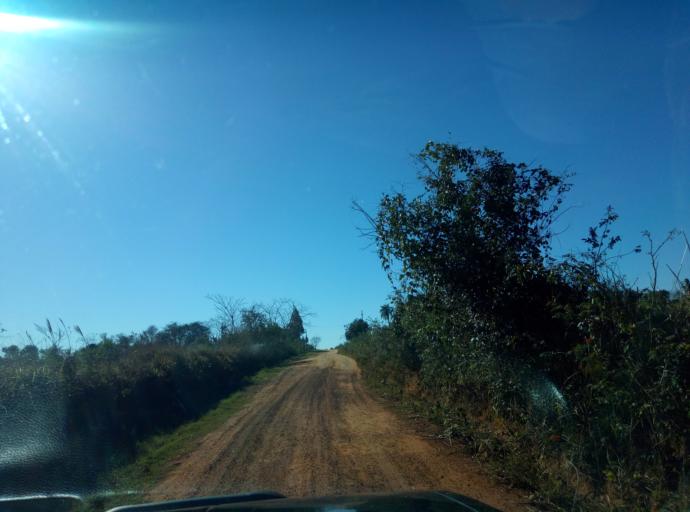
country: PY
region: Caaguazu
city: Doctor Cecilio Baez
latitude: -25.1646
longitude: -56.2334
